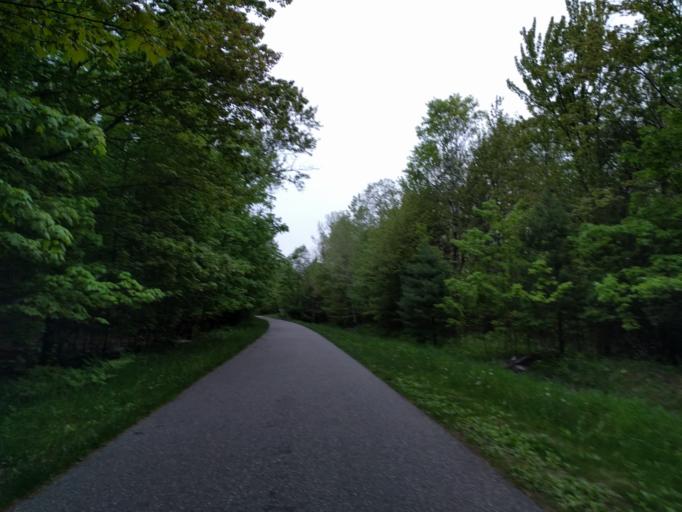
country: US
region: Michigan
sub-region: Marquette County
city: Trowbridge Park
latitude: 46.5537
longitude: -87.4171
